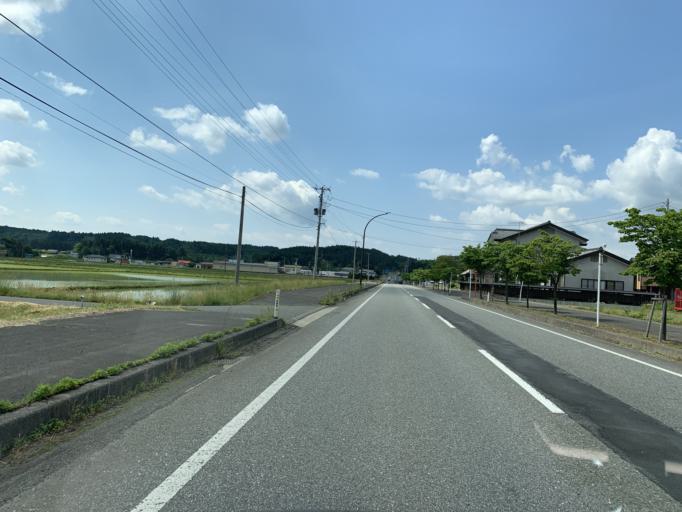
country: JP
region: Miyagi
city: Furukawa
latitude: 38.7378
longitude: 140.9596
